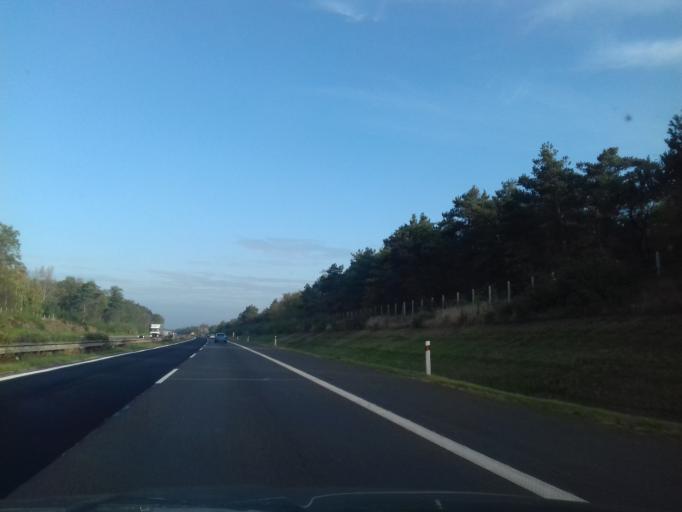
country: SK
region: Bratislavsky
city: Stupava
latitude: 48.3353
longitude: 17.0242
